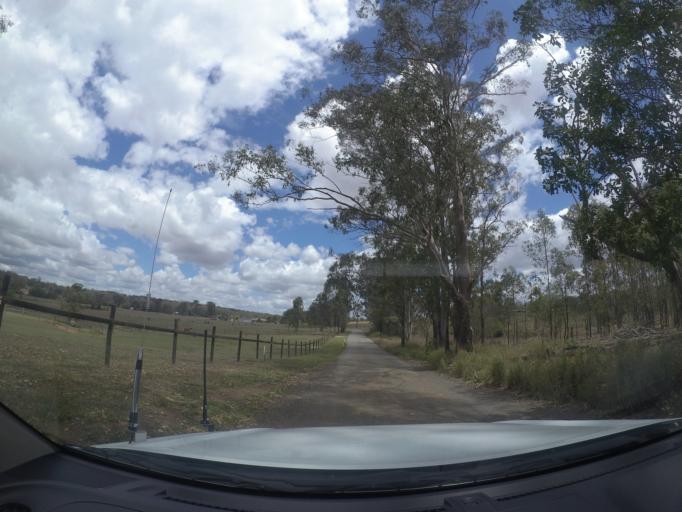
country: AU
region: Queensland
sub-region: Logan
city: Cedar Vale
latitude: -27.9392
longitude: 153.0668
